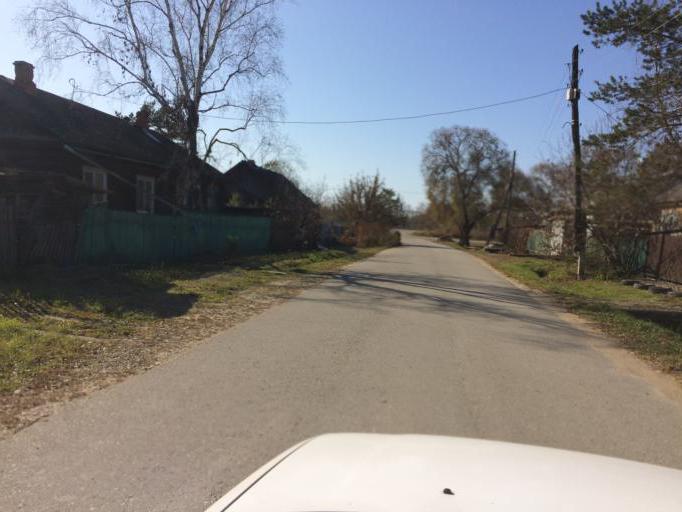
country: RU
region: Primorskiy
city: Dal'nerechensk
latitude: 45.9115
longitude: 133.8036
